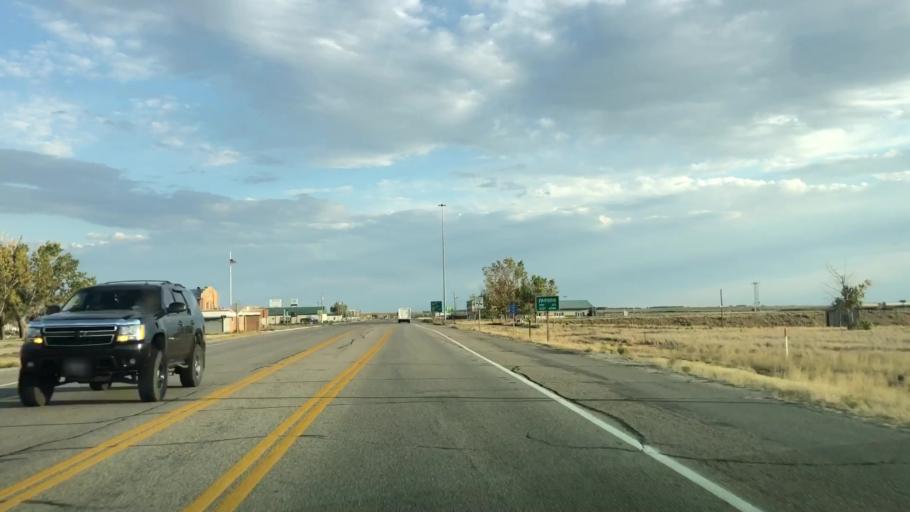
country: US
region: Wyoming
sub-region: Sweetwater County
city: North Rock Springs
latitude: 42.1108
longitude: -109.4498
